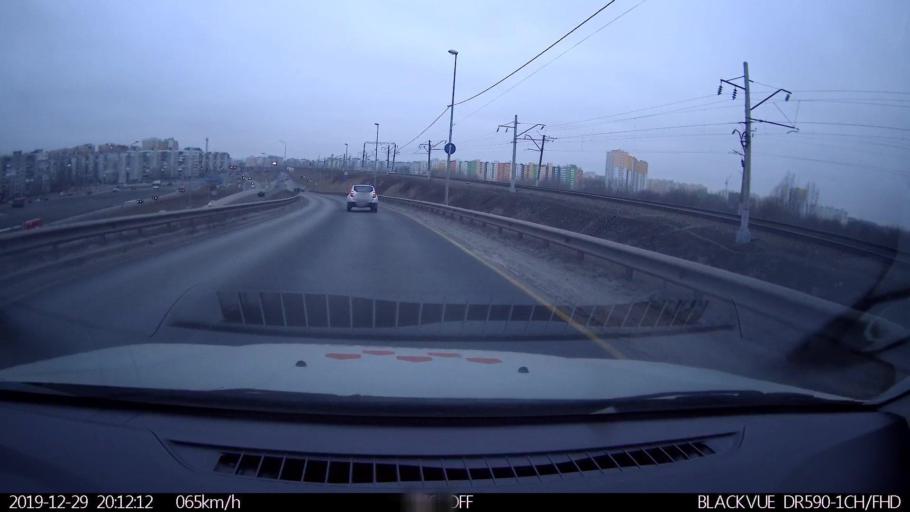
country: RU
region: Nizjnij Novgorod
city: Nizhniy Novgorod
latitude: 56.3486
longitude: 43.9216
